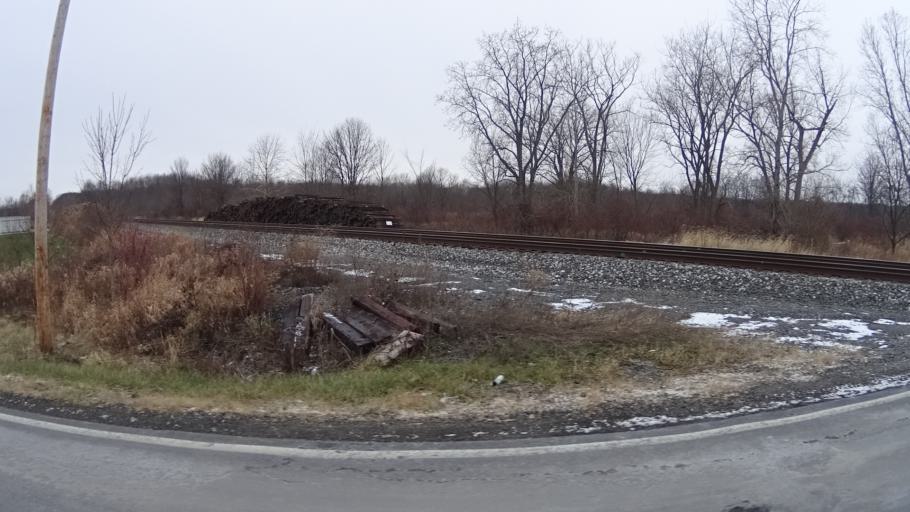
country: US
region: Ohio
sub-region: Lorain County
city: Lagrange
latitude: 41.2091
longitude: -82.1580
